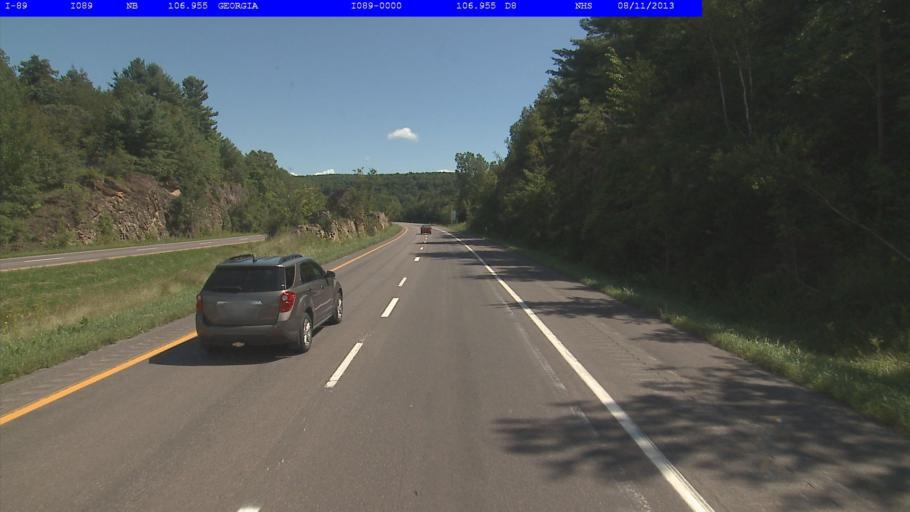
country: US
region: Vermont
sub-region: Chittenden County
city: Milton
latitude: 44.7011
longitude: -73.0991
